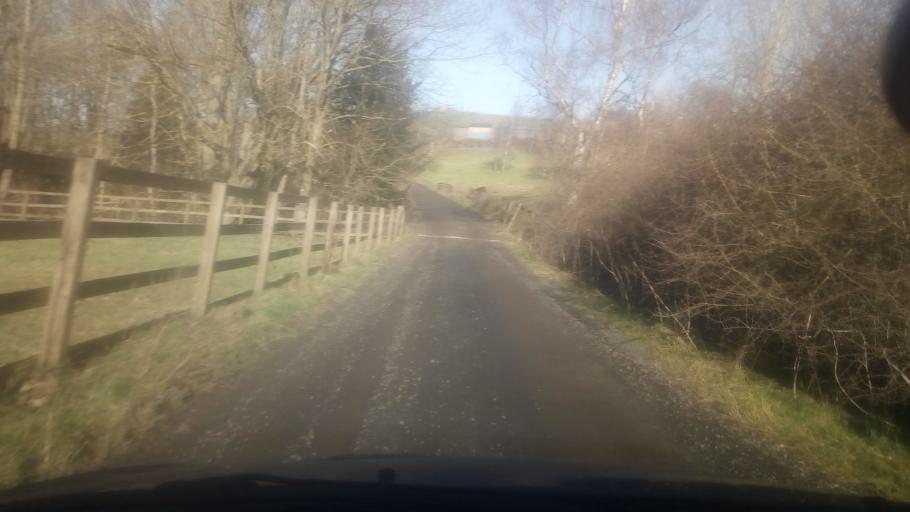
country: GB
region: Scotland
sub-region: The Scottish Borders
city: Jedburgh
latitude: 55.4846
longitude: -2.5355
